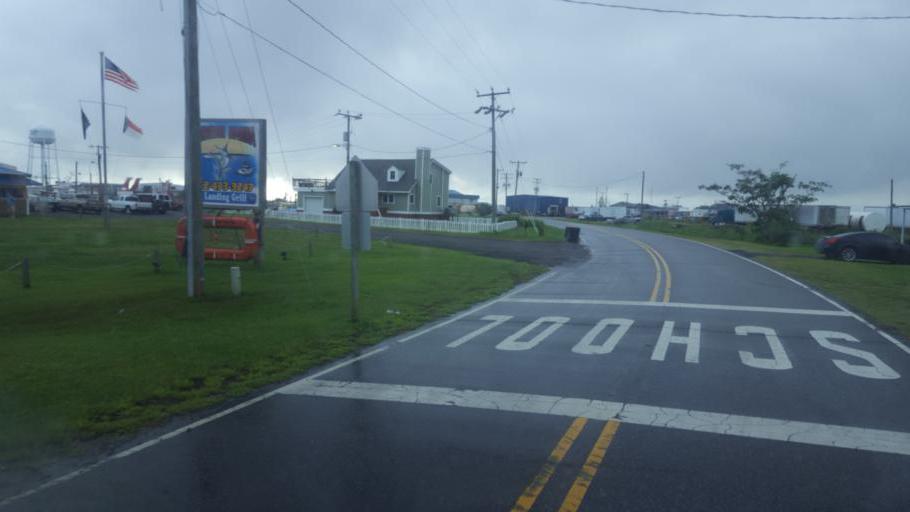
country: US
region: North Carolina
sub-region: Dare County
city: Wanchese
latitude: 35.8415
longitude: -75.6235
